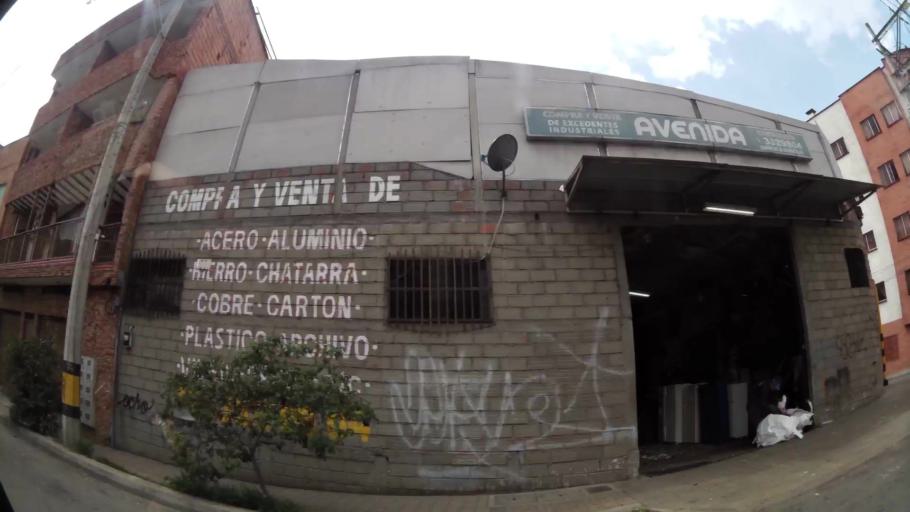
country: CO
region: Antioquia
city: Envigado
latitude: 6.1651
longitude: -75.5947
